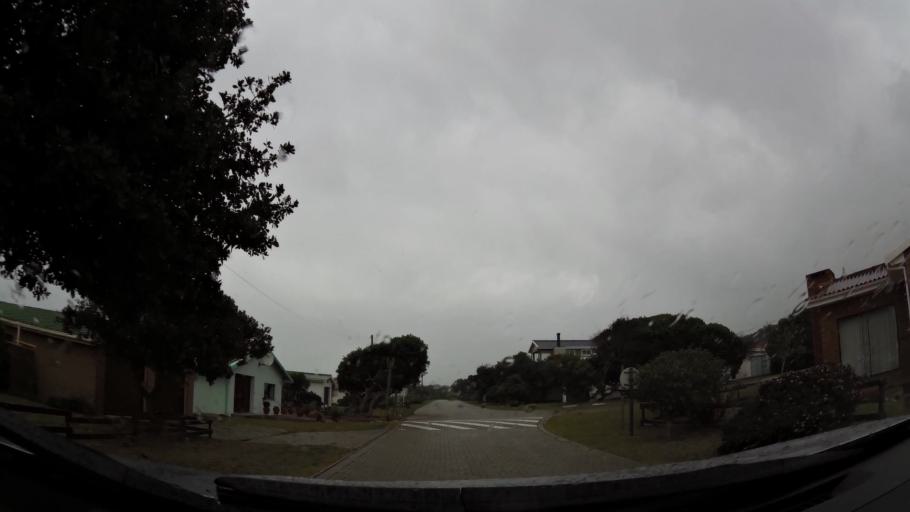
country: ZA
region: Western Cape
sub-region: Eden District Municipality
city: Mossel Bay
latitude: -34.0515
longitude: 22.2694
